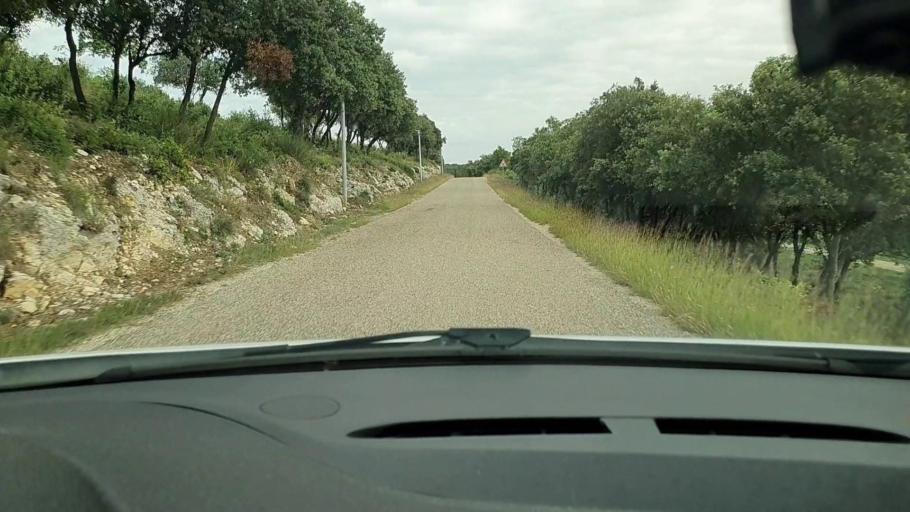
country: FR
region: Languedoc-Roussillon
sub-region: Departement du Gard
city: Montaren-et-Saint-Mediers
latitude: 44.1067
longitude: 4.3023
